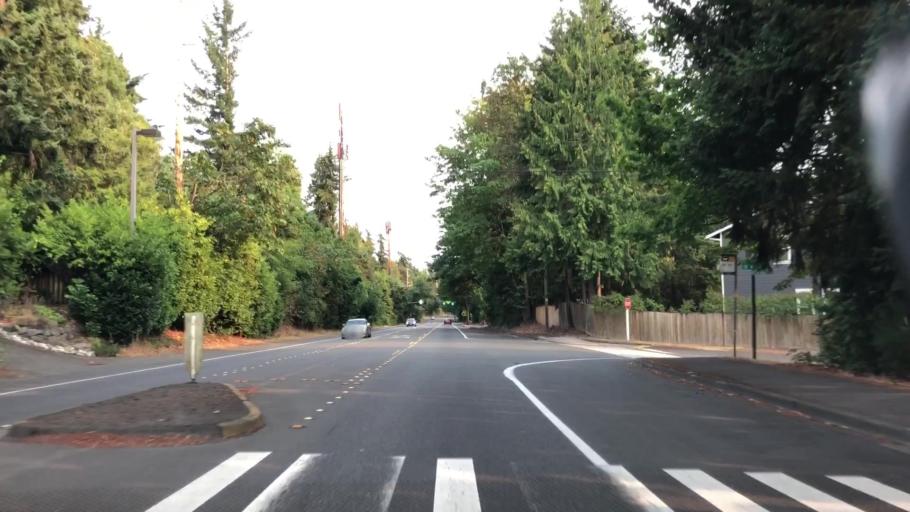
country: US
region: Washington
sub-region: King County
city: Mercer Island
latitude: 47.5640
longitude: -122.2241
